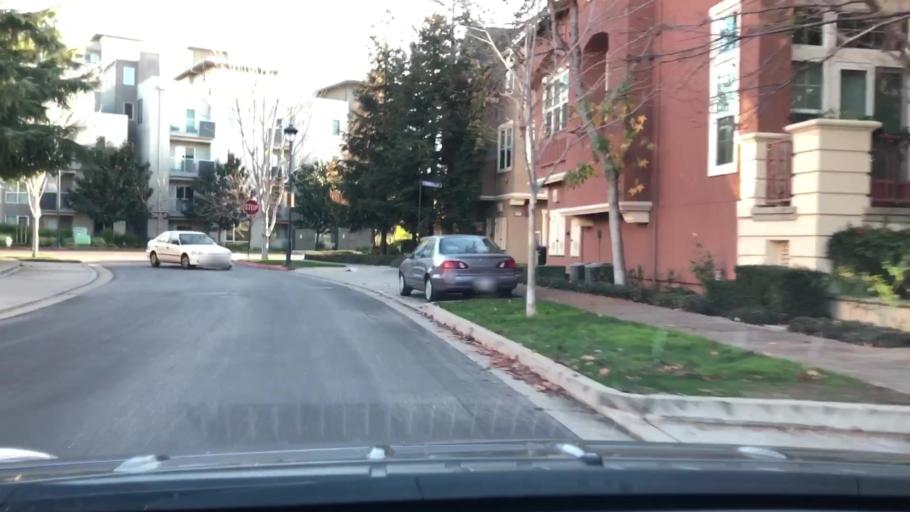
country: US
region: California
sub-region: Santa Clara County
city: Santa Clara
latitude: 37.3966
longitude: -121.9454
